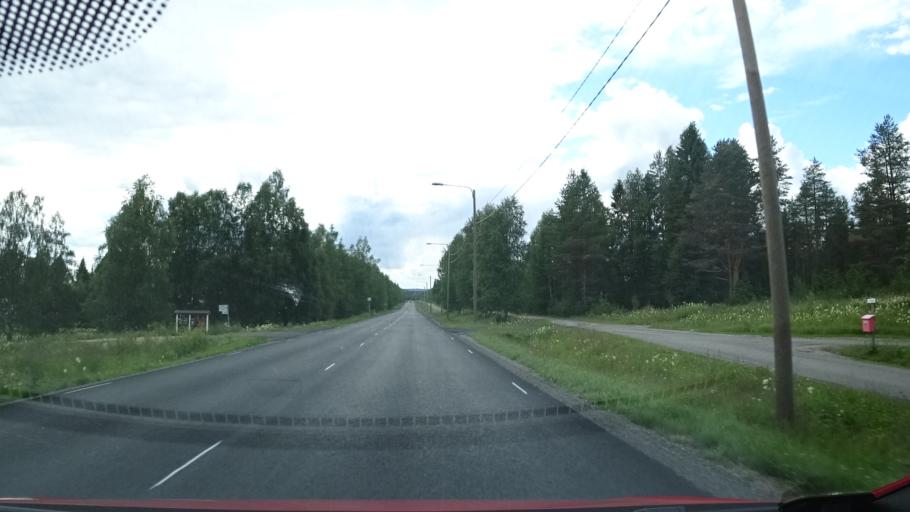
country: FI
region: Lapland
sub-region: Rovaniemi
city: Rovaniemi
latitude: 66.4326
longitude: 25.4580
